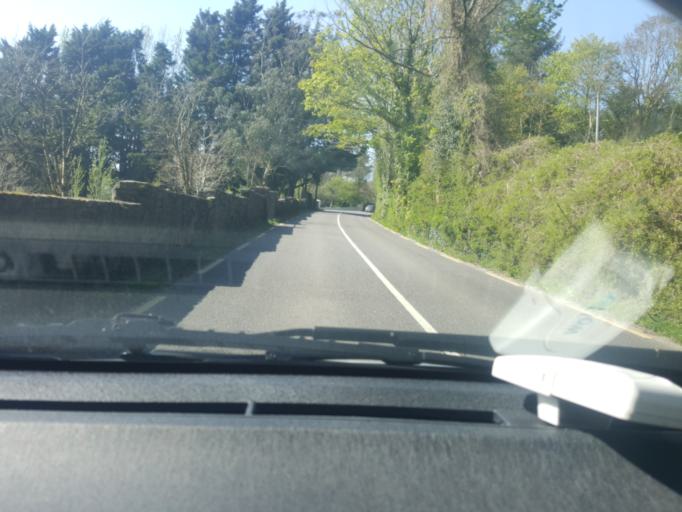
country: IE
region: Munster
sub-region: County Cork
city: Bandon
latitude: 51.7595
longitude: -8.6462
